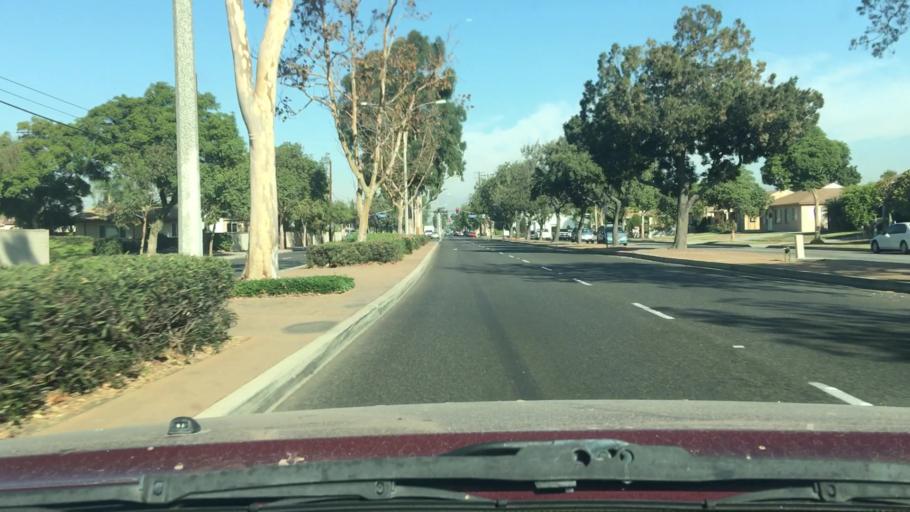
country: US
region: California
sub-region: Los Angeles County
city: Norwalk
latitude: 33.9081
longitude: -118.0992
